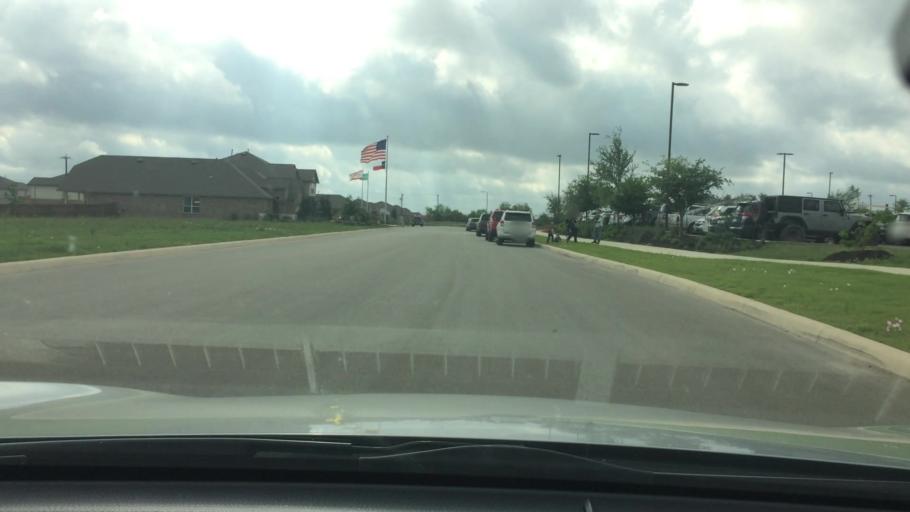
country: US
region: Texas
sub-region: Bexar County
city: Helotes
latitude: 29.5197
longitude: -98.7659
